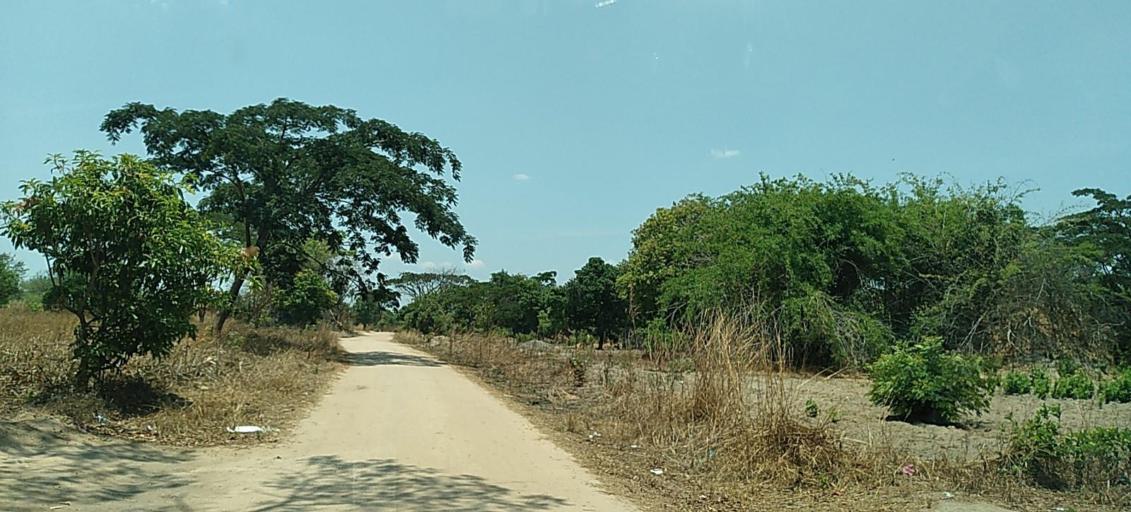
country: ZM
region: Copperbelt
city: Luanshya
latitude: -13.0789
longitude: 28.4051
